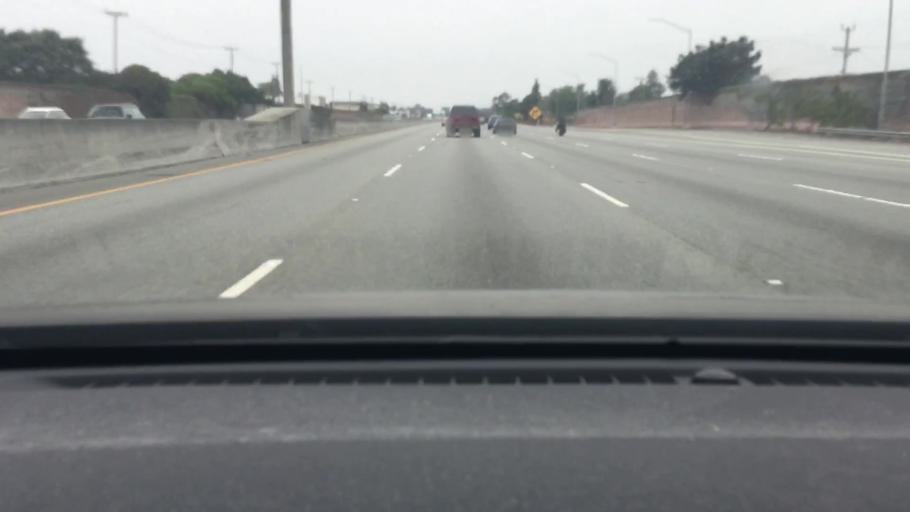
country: US
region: California
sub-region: San Mateo County
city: San Mateo
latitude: 37.5614
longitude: -122.3048
